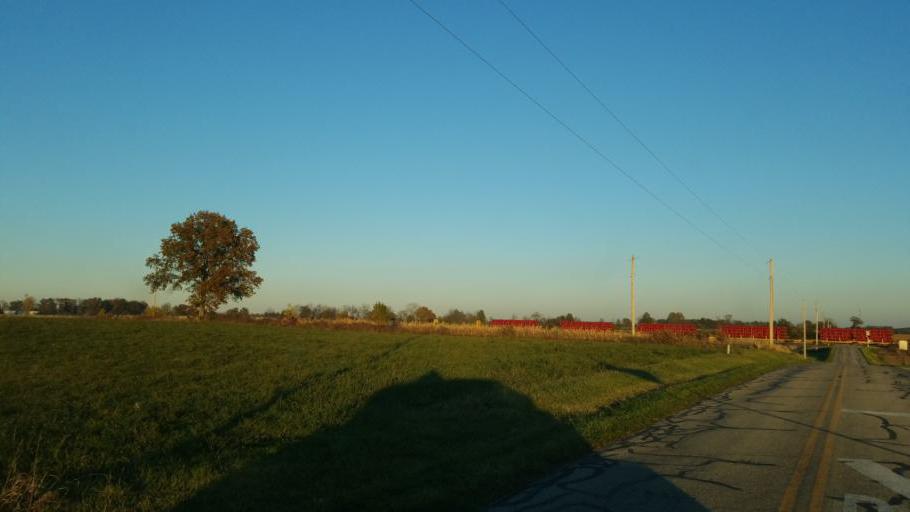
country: US
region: Ohio
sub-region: Huron County
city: Bellevue
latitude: 41.2117
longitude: -82.8726
